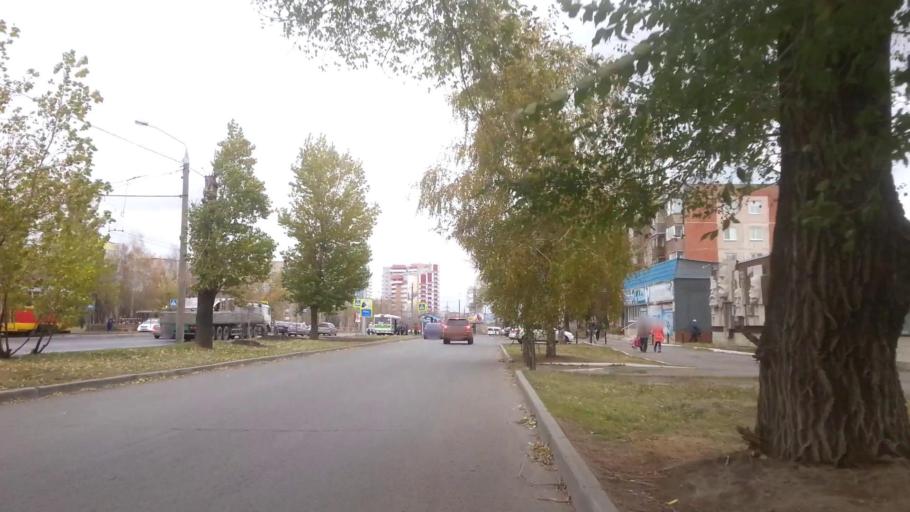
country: RU
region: Altai Krai
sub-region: Gorod Barnaulskiy
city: Barnaul
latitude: 53.3657
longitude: 83.7061
